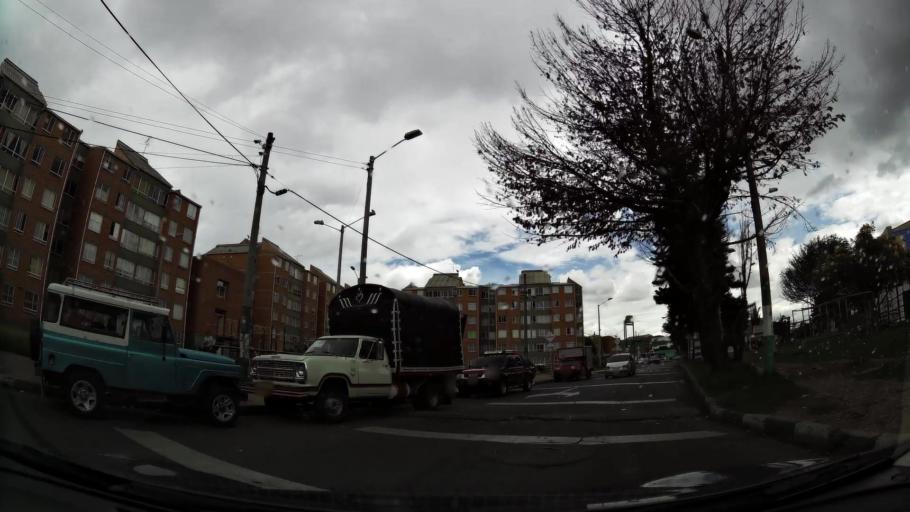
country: CO
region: Bogota D.C.
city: Barrio San Luis
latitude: 4.7056
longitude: -74.0894
